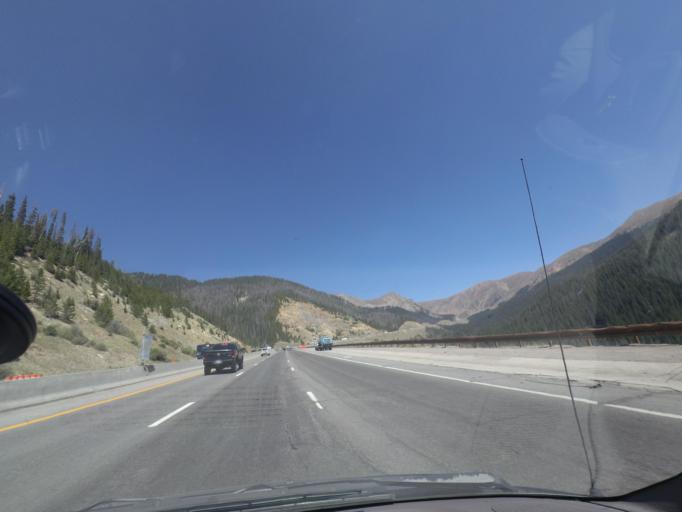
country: US
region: Colorado
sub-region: Summit County
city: Keystone
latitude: 39.6698
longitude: -105.9746
